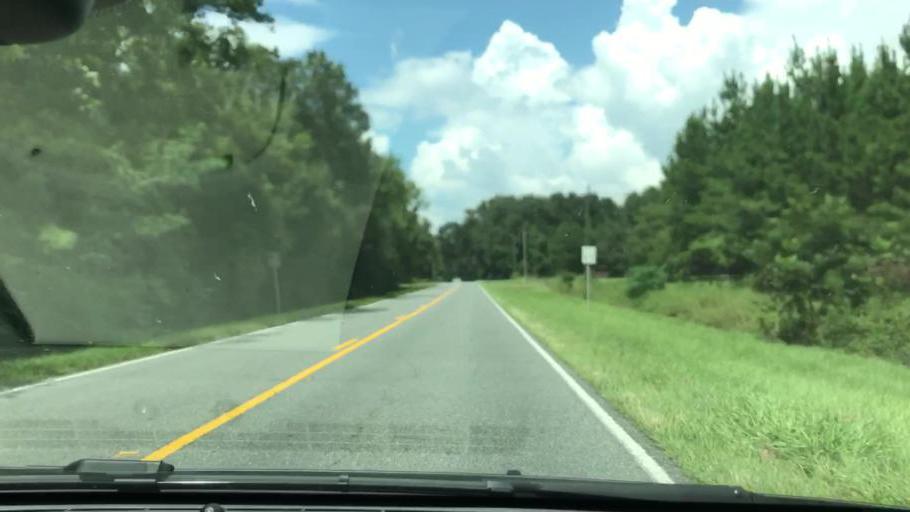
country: US
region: Florida
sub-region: Jackson County
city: Malone
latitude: 30.9388
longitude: -85.1184
